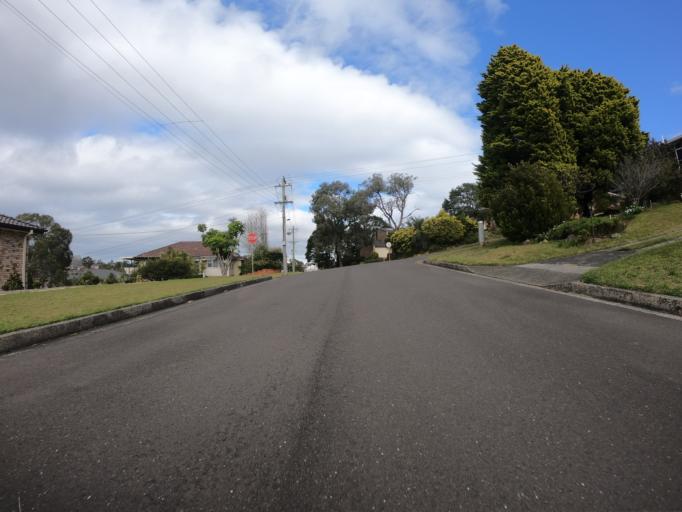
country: AU
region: New South Wales
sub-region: Wollongong
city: Mount Ousley
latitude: -34.3971
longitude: 150.8781
